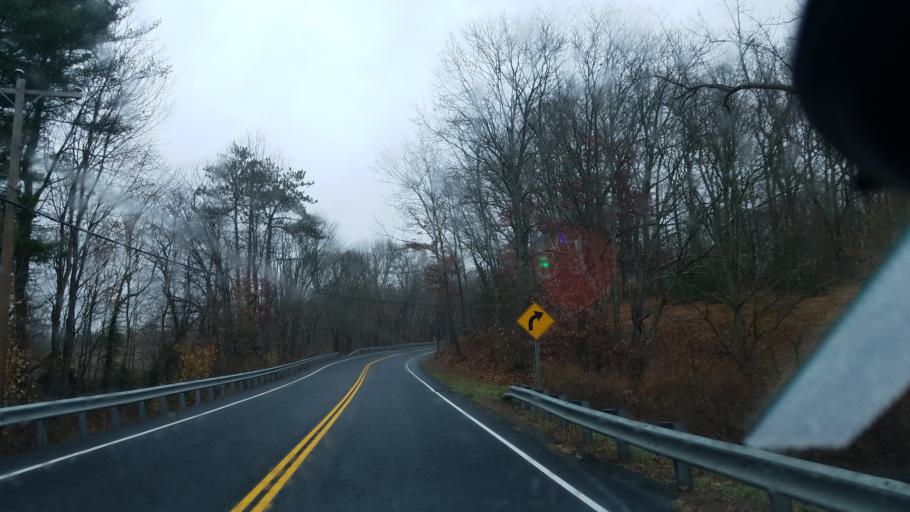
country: US
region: Connecticut
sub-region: Litchfield County
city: Watertown
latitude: 41.6007
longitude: -73.1570
